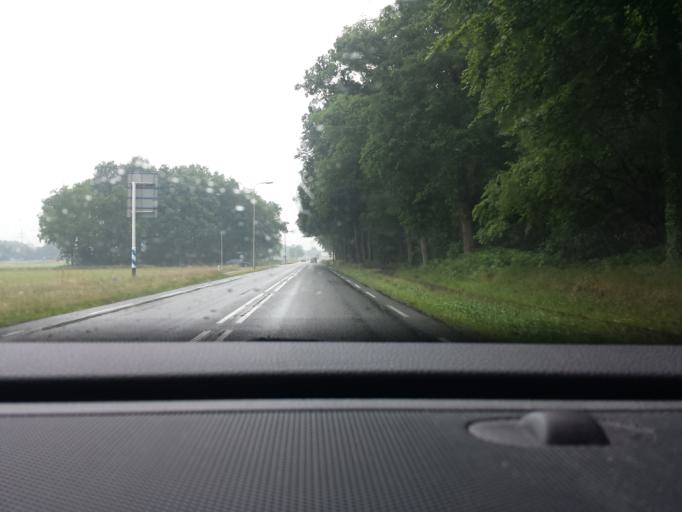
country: NL
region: Gelderland
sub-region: Berkelland
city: Eibergen
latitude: 52.1365
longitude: 6.6857
